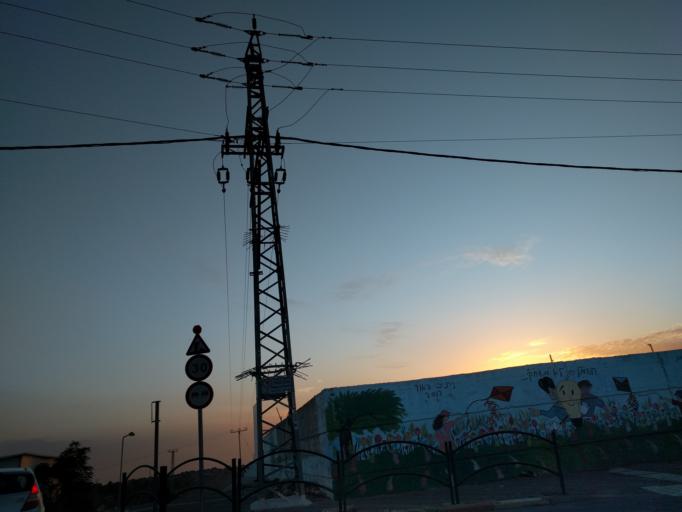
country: IL
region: Haifa
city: Daliyat el Karmil
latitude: 32.6878
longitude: 35.0579
